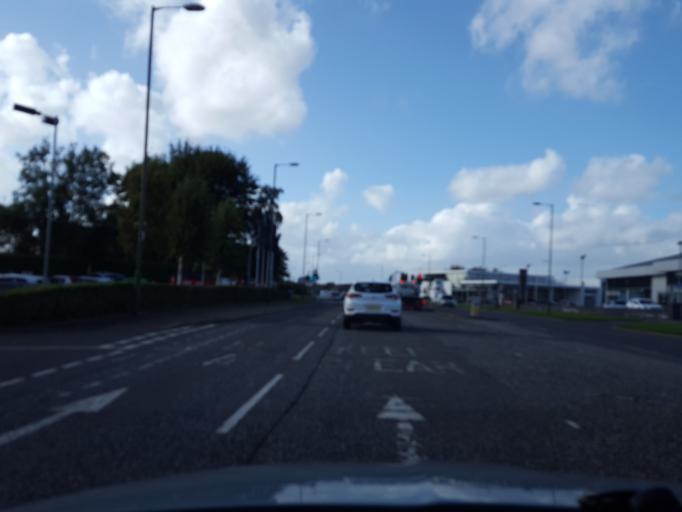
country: GB
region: Scotland
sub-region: Edinburgh
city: Newbridge
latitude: 55.9401
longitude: -3.4064
